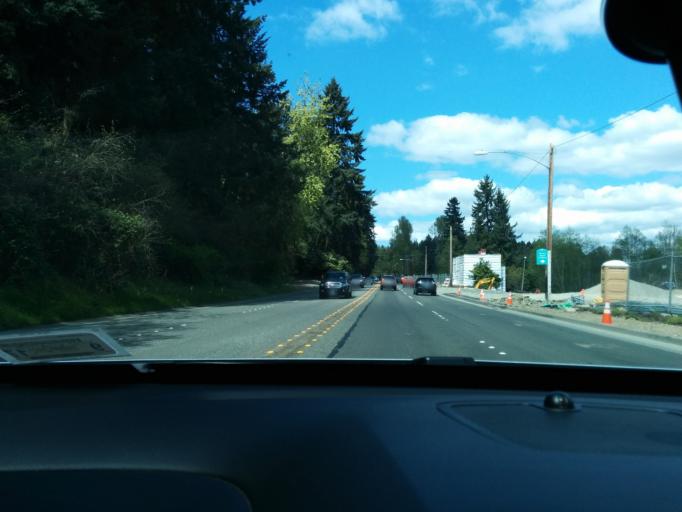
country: US
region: Washington
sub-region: King County
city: Bellevue
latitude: 47.5901
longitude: -122.1926
